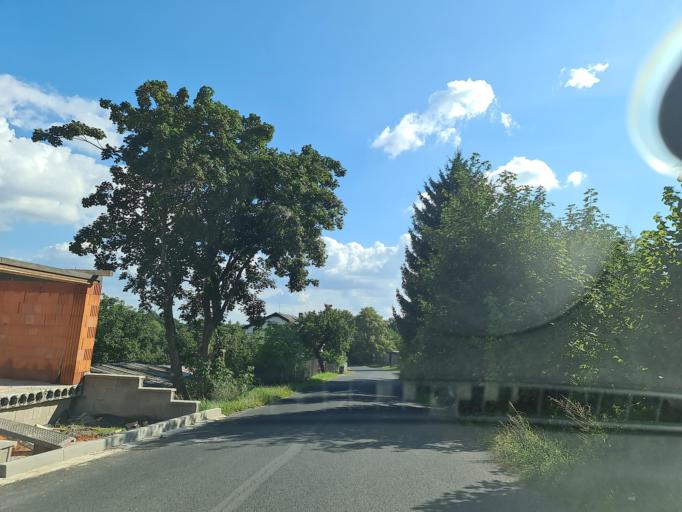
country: CZ
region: Ustecky
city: Horni Jiretin
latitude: 50.6045
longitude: 13.5549
